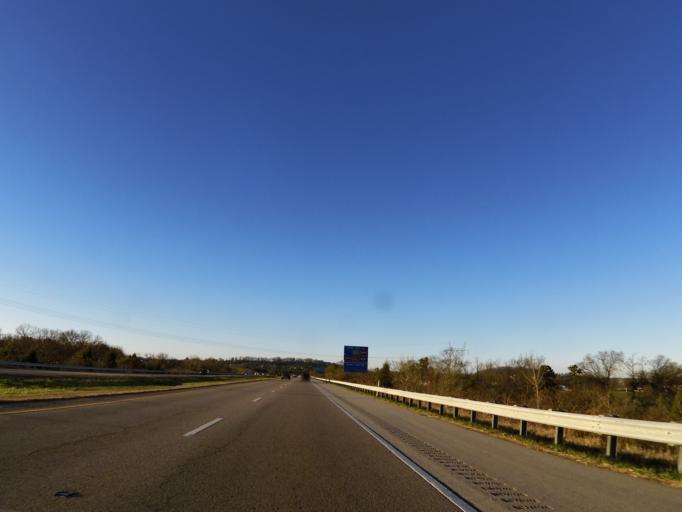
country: US
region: Tennessee
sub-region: Blount County
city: Eagleton Village
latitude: 35.8203
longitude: -83.9523
